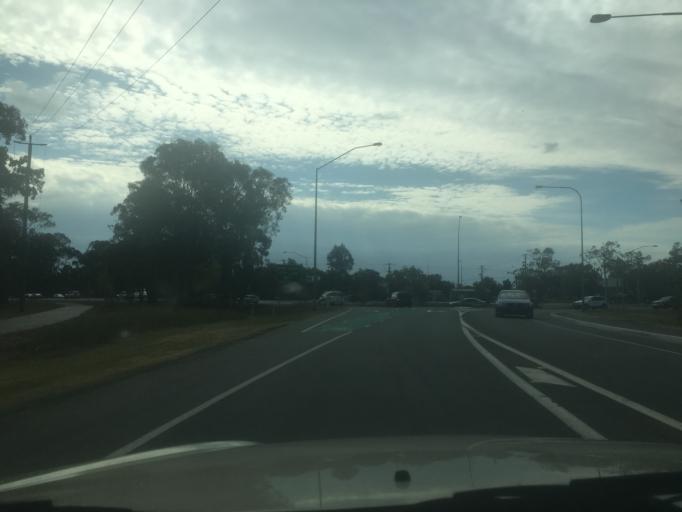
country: AU
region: Queensland
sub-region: Moreton Bay
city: Bongaree
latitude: -27.0647
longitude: 153.1559
